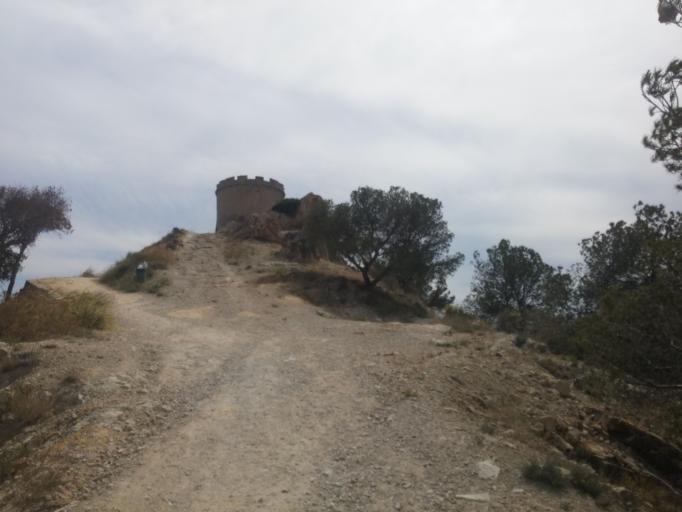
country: ES
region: Valencia
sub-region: Provincia de Alicante
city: Villajoyosa
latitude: 38.4999
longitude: -0.2471
